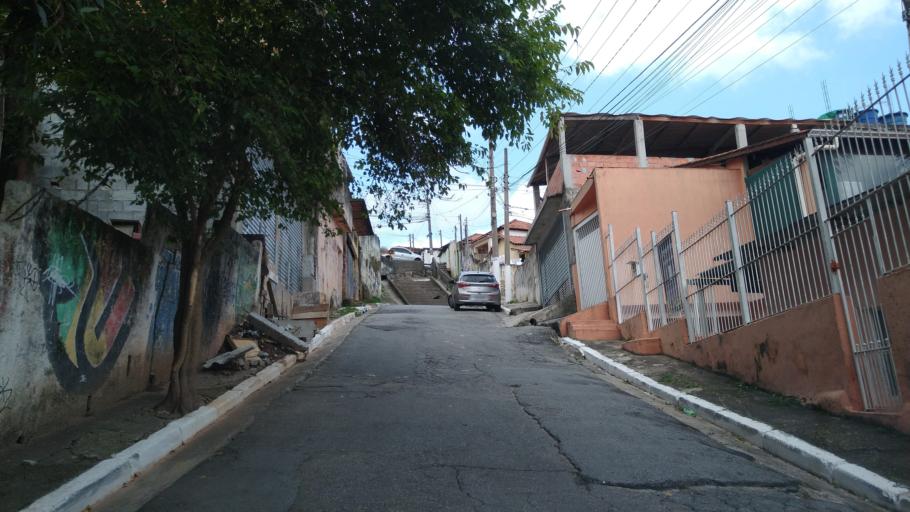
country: BR
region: Sao Paulo
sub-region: Sao Paulo
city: Sao Paulo
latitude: -23.4822
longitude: -46.6400
